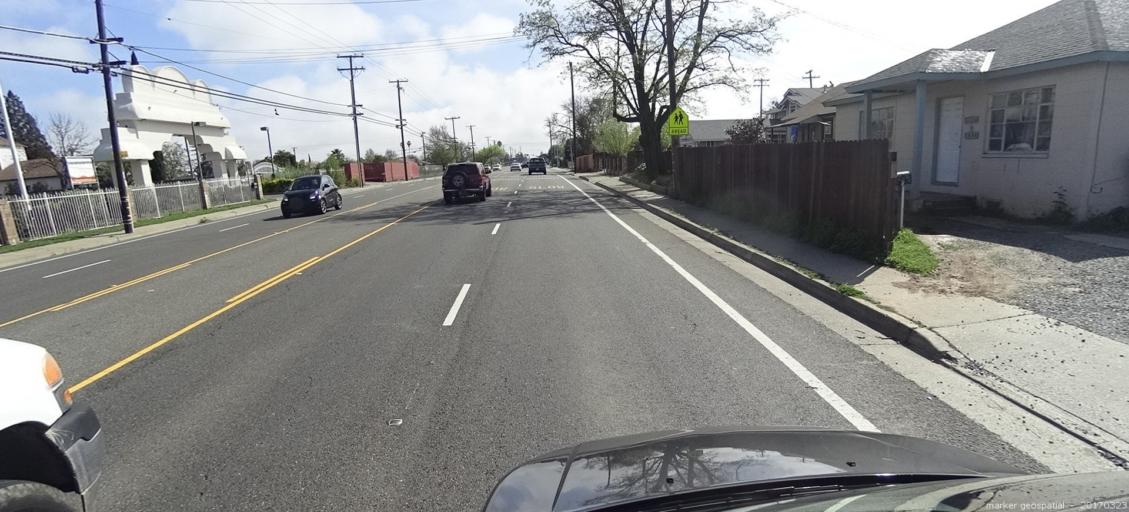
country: US
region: California
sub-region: Sacramento County
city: Florin
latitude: 38.5105
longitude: -121.4171
